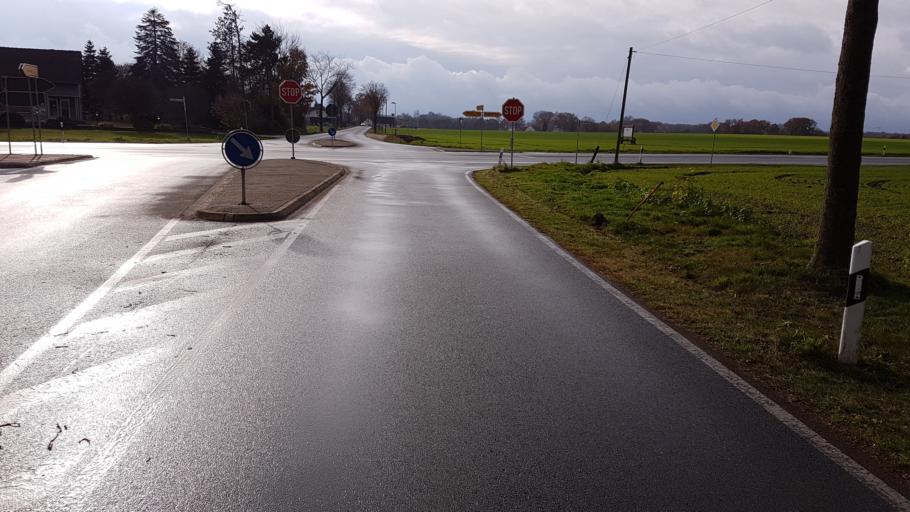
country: DE
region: North Rhine-Westphalia
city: Espelkamp
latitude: 52.3925
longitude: 8.5526
